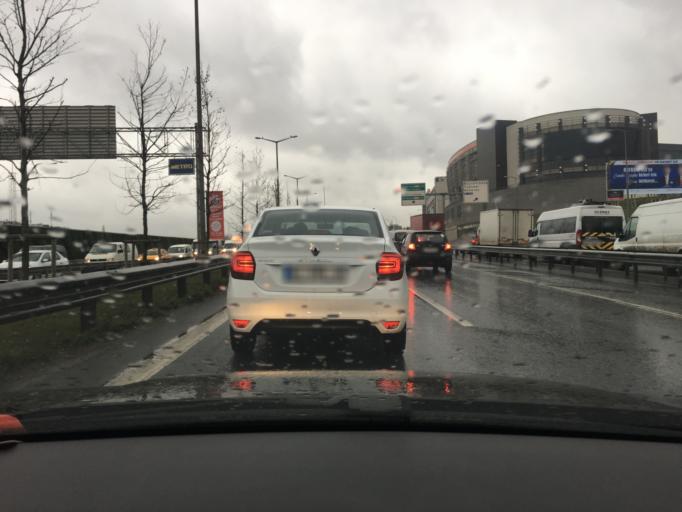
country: TR
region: Istanbul
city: Esenler
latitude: 41.0399
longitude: 28.8871
